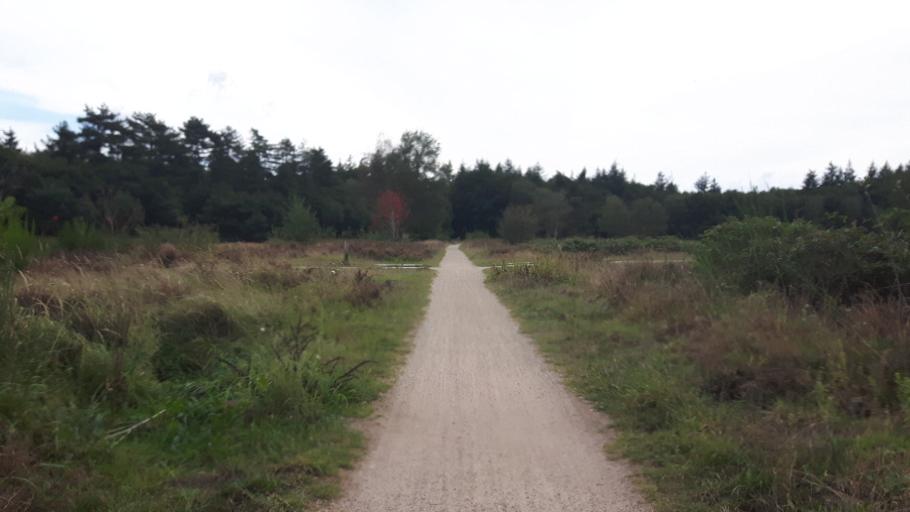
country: NL
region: Gelderland
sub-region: Gemeente Ermelo
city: Ermelo
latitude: 52.2827
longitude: 5.6146
